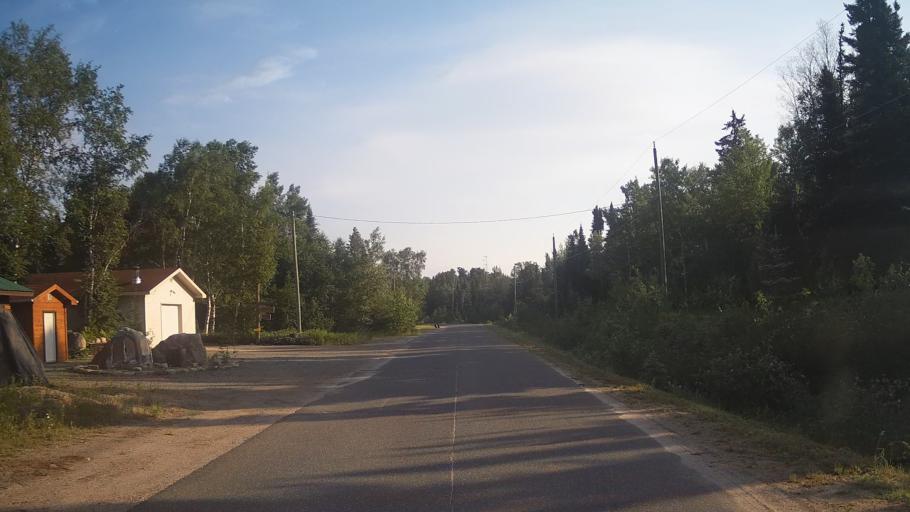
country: CA
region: Ontario
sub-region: Rainy River District
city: Atikokan
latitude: 49.4001
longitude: -91.6659
